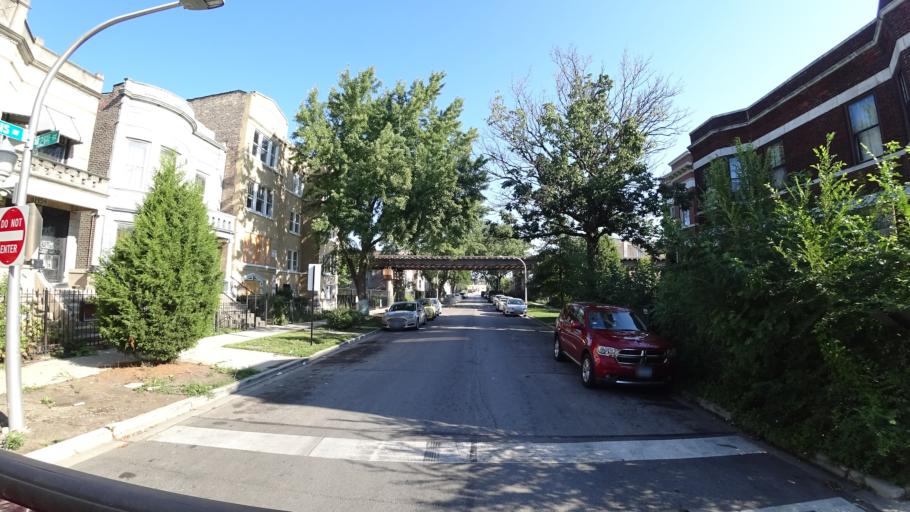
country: US
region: Illinois
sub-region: Cook County
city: Cicero
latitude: 41.8537
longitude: -87.7124
